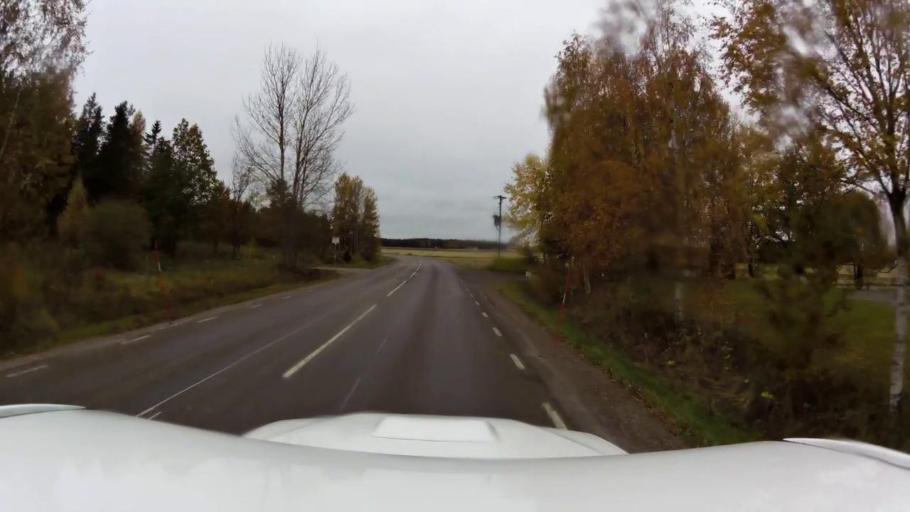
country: SE
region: OEstergoetland
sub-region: Linkopings Kommun
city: Linghem
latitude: 58.4391
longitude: 15.7147
